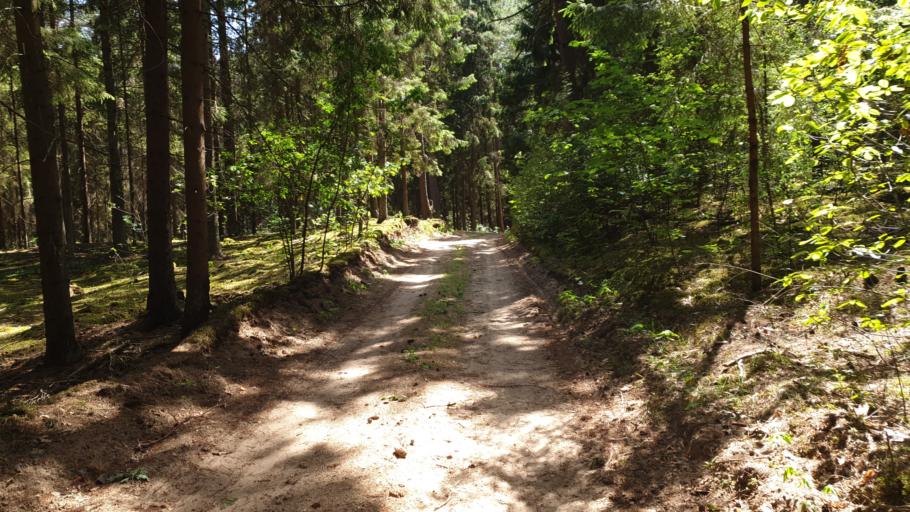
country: LT
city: Grigiskes
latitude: 54.7774
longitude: 24.9931
